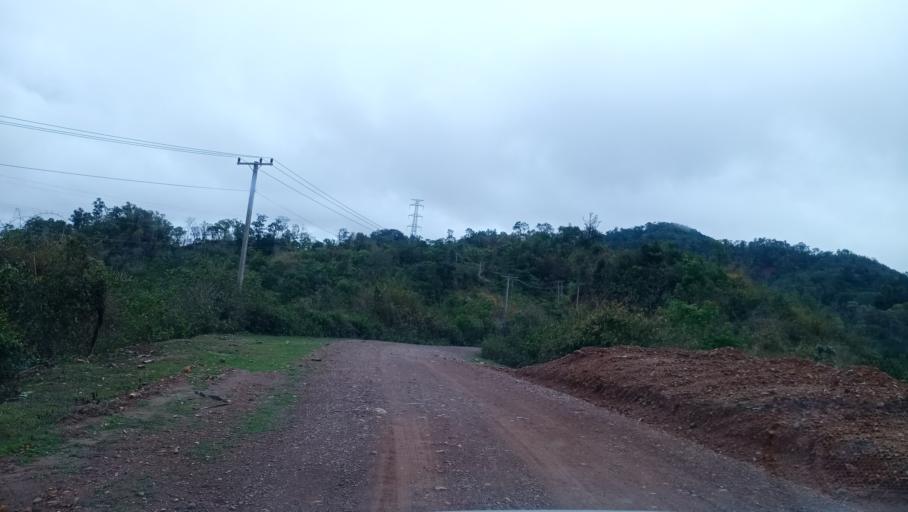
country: LA
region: Phongsali
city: Phongsali
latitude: 21.3423
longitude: 102.0881
